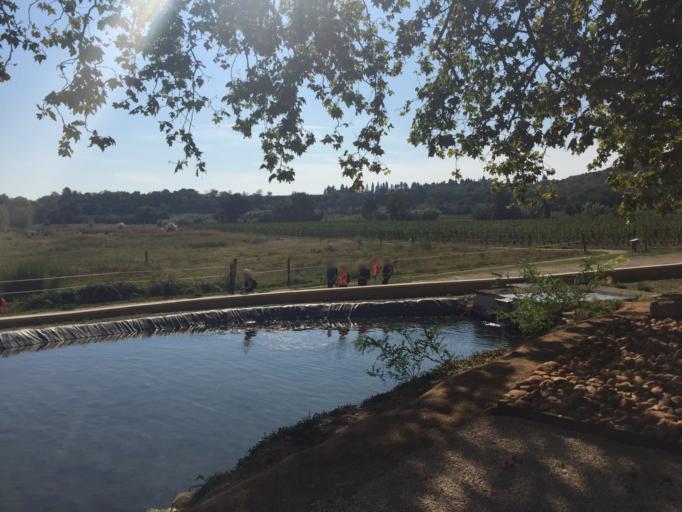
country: FR
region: Provence-Alpes-Cote d'Azur
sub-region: Departement du Vaucluse
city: Courthezon
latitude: 44.0717
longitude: 4.8642
